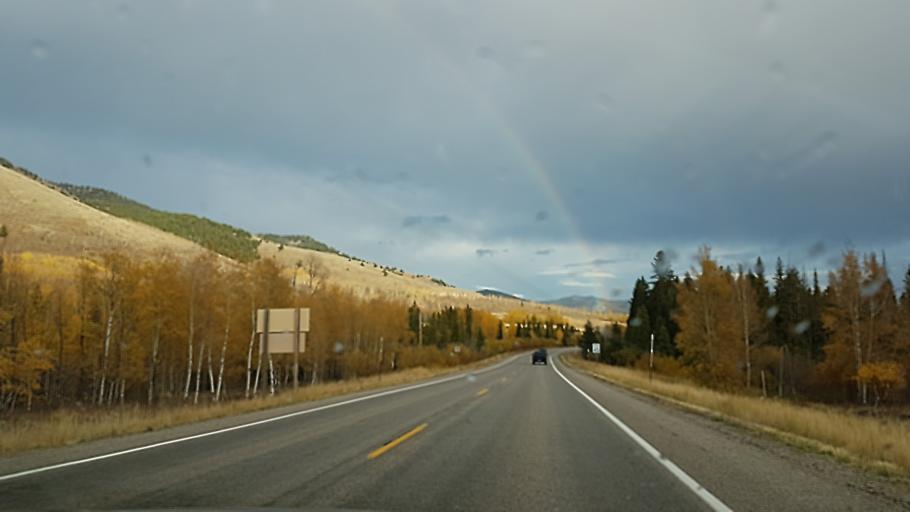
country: US
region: Montana
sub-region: Gallatin County
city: West Yellowstone
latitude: 44.6732
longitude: -111.4078
